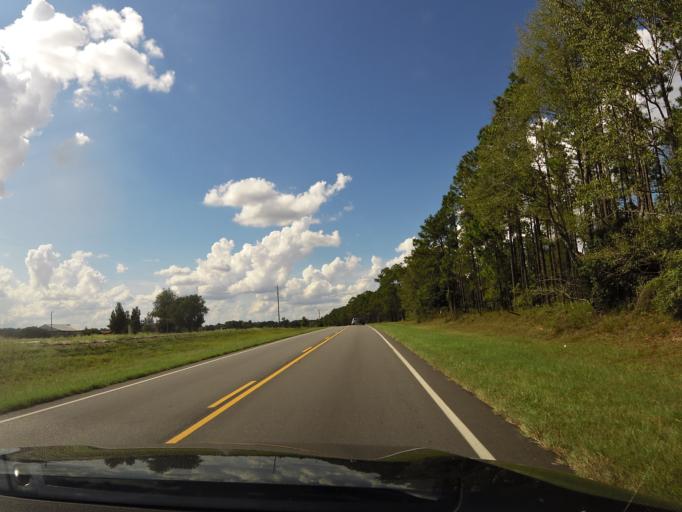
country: US
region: Georgia
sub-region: Echols County
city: Statenville
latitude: 30.7627
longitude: -83.1254
